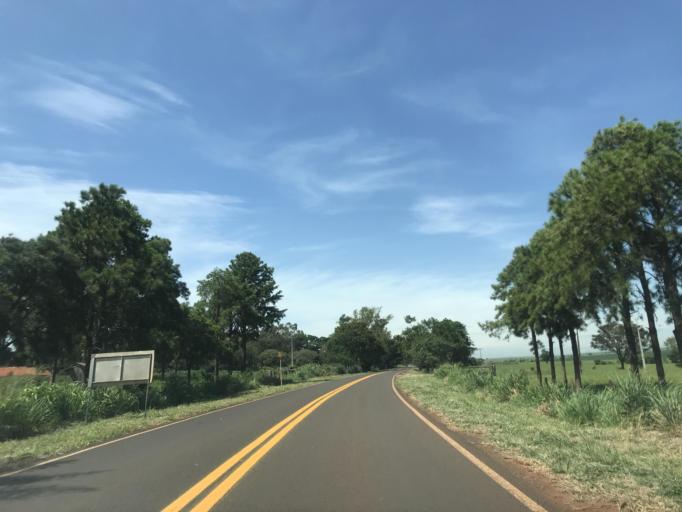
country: BR
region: Parana
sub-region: Terra Rica
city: Terra Rica
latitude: -22.7947
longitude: -52.6529
